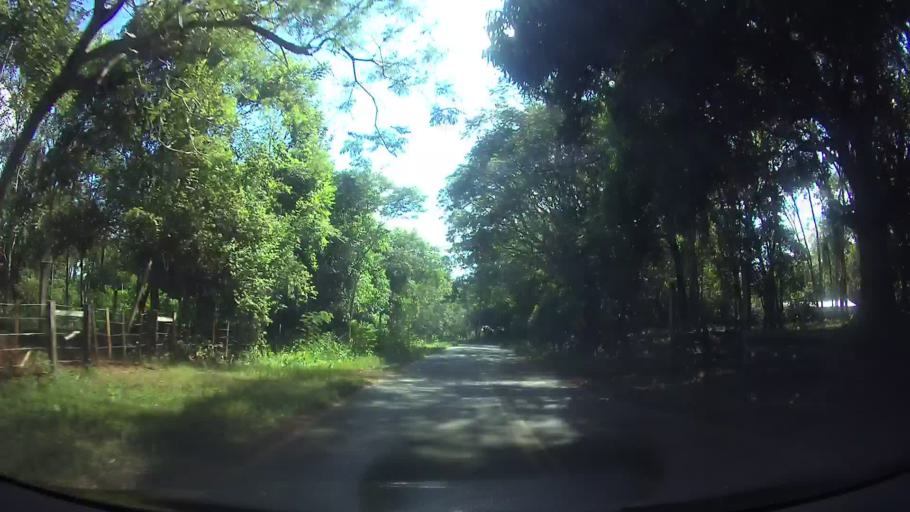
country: PY
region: Paraguari
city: Sapucai
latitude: -25.6686
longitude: -56.8592
